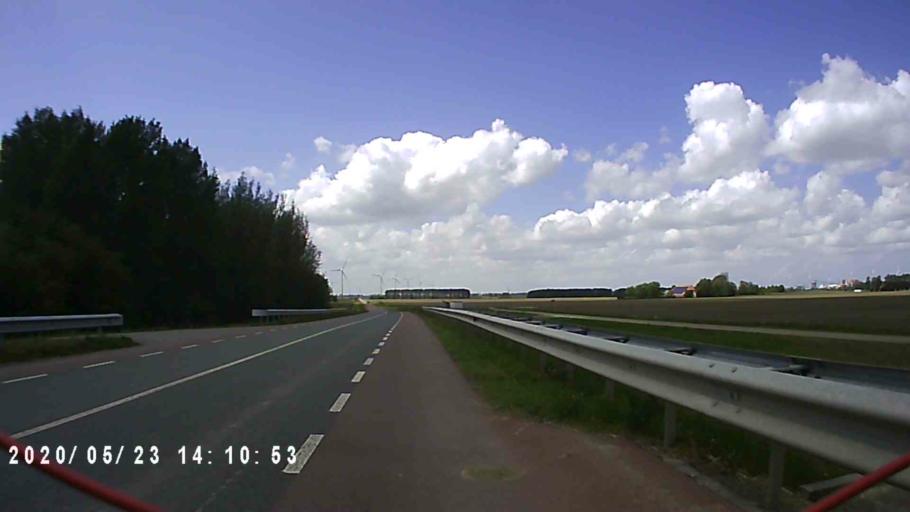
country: NL
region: Groningen
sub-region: Gemeente Delfzijl
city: Delfzijl
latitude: 53.2861
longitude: 7.0141
